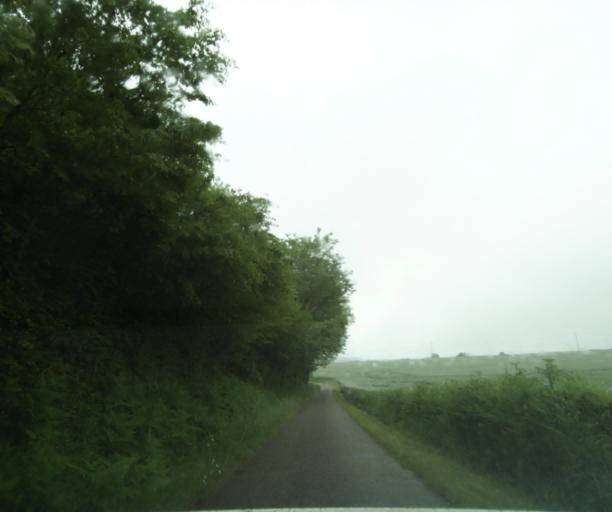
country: FR
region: Bourgogne
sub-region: Departement de Saone-et-Loire
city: Charolles
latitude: 46.4378
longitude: 4.3801
